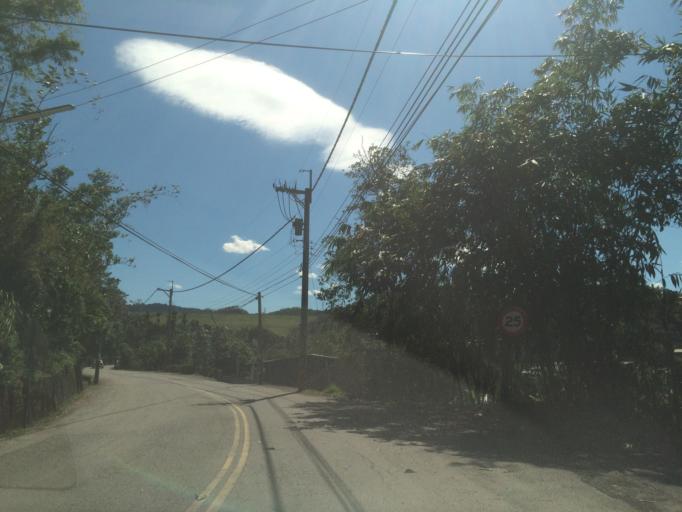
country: TW
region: Taiwan
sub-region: Yunlin
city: Douliu
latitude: 23.6964
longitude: 120.6206
